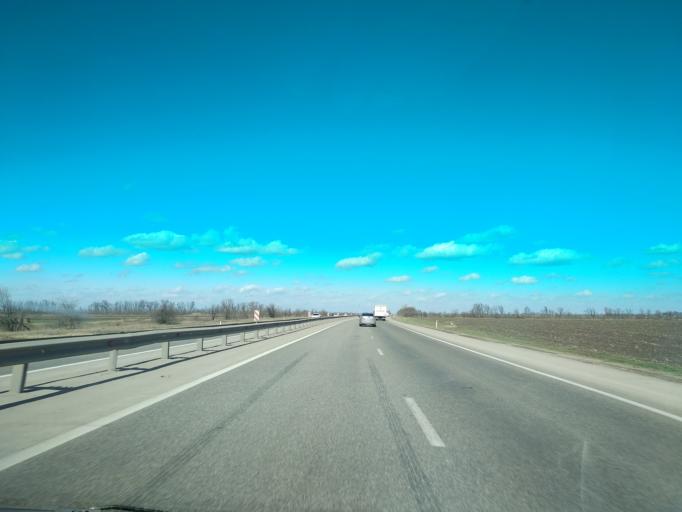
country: RU
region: Krasnodarskiy
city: Agronom
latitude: 45.1270
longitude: 39.1101
